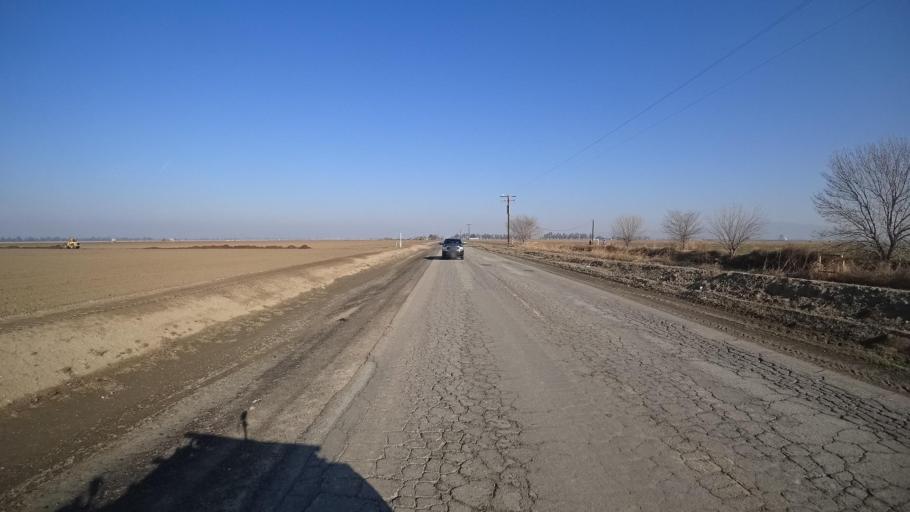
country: US
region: California
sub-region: Kern County
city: Weedpatch
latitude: 35.1717
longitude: -118.9678
